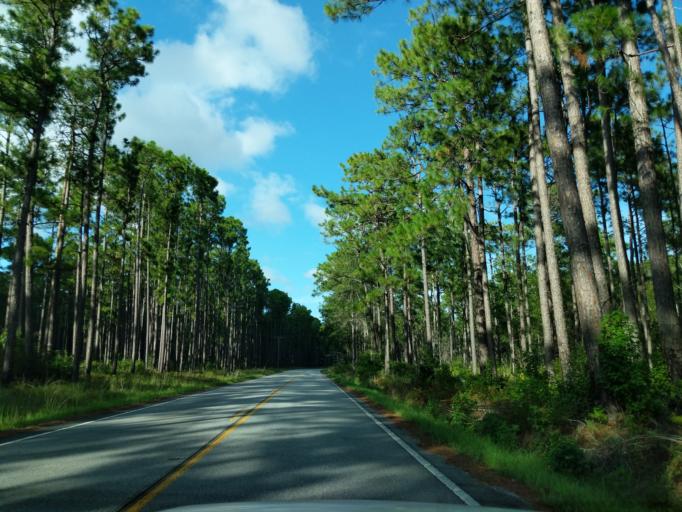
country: US
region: South Carolina
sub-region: Charleston County
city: Awendaw
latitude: 33.1313
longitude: -79.4442
